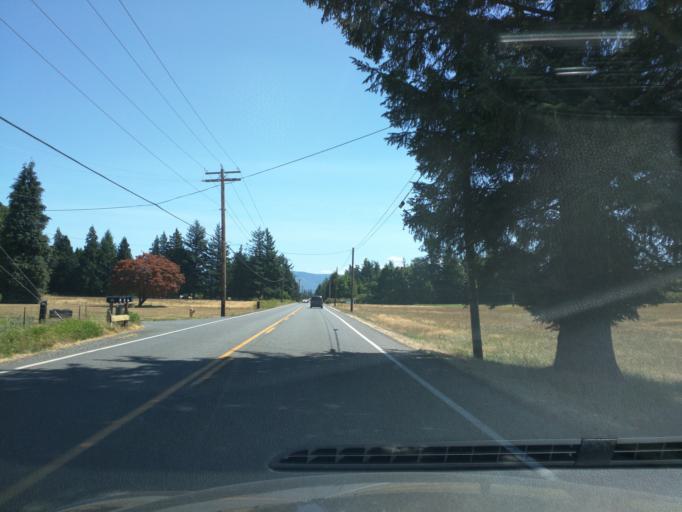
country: US
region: Washington
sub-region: Whatcom County
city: Lynden
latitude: 48.8917
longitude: -122.4569
